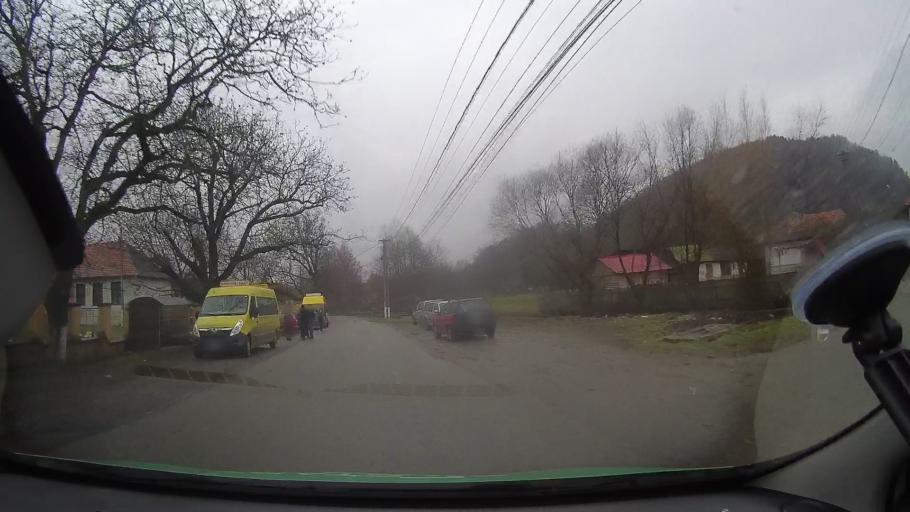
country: RO
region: Arad
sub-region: Comuna Halmagel
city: Halmagel
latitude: 46.2682
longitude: 22.6214
